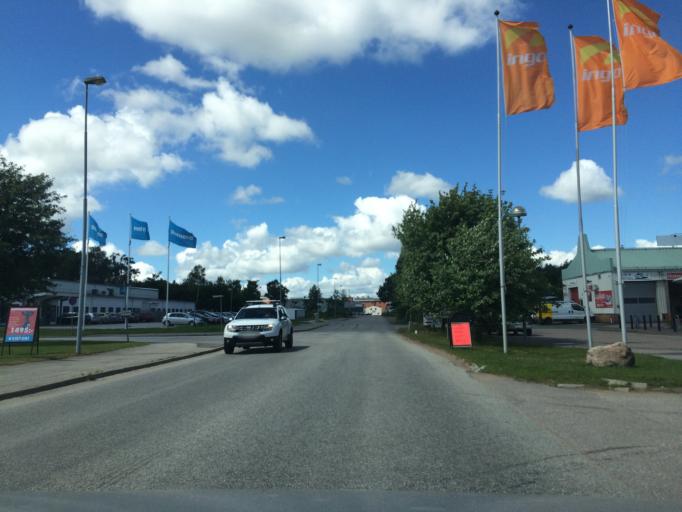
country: SE
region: Vaestra Goetaland
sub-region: Trollhattan
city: Trollhattan
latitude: 58.2984
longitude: 12.3214
